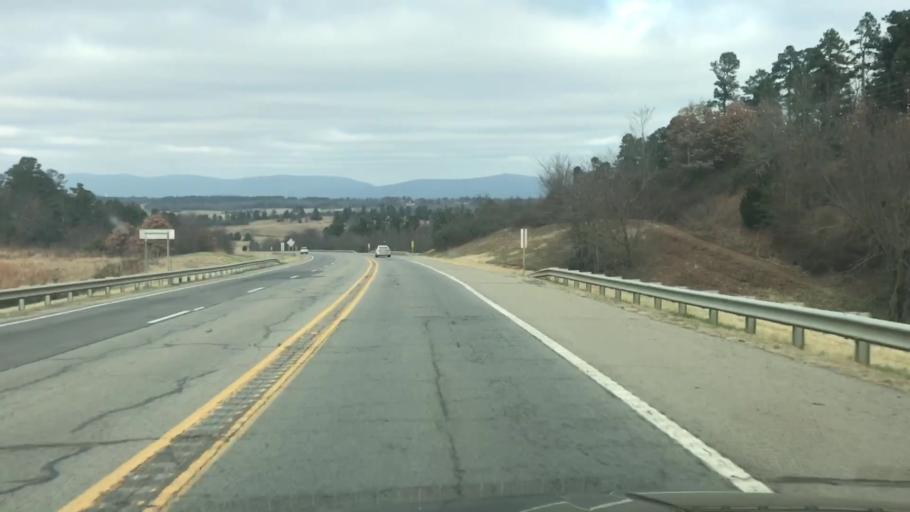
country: US
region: Arkansas
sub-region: Scott County
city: Waldron
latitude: 34.8650
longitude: -94.0744
